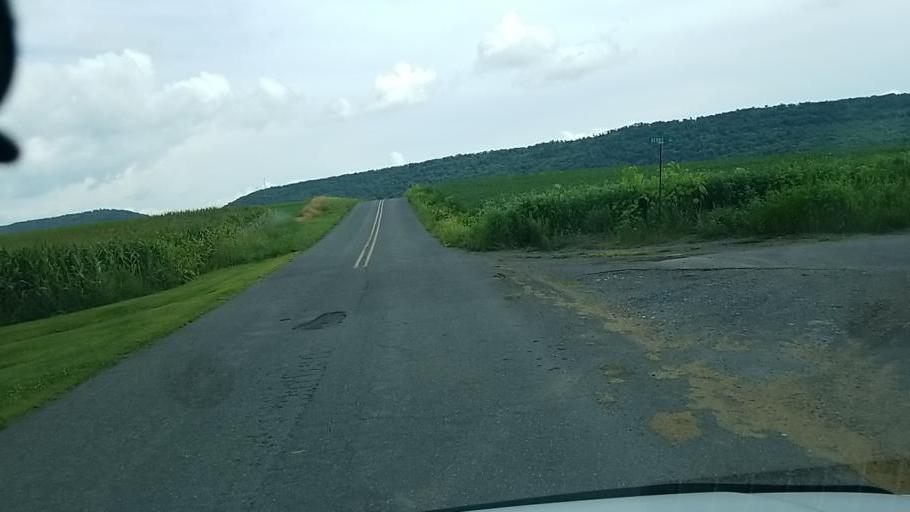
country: US
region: Pennsylvania
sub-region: Dauphin County
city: Elizabethville
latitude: 40.6432
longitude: -76.8248
